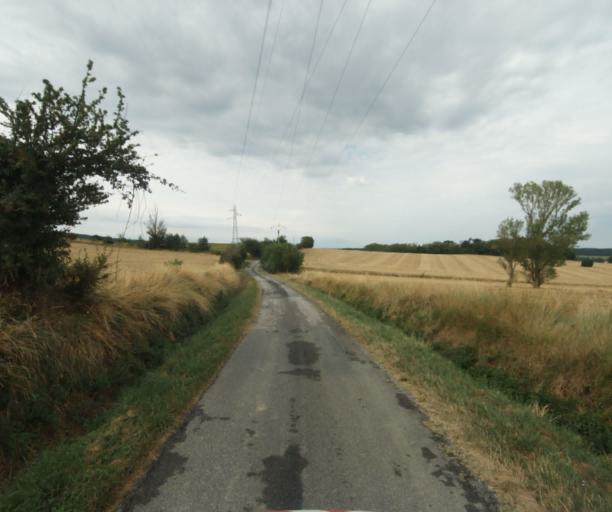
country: FR
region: Midi-Pyrenees
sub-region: Departement de la Haute-Garonne
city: Revel
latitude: 43.4295
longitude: 1.9654
